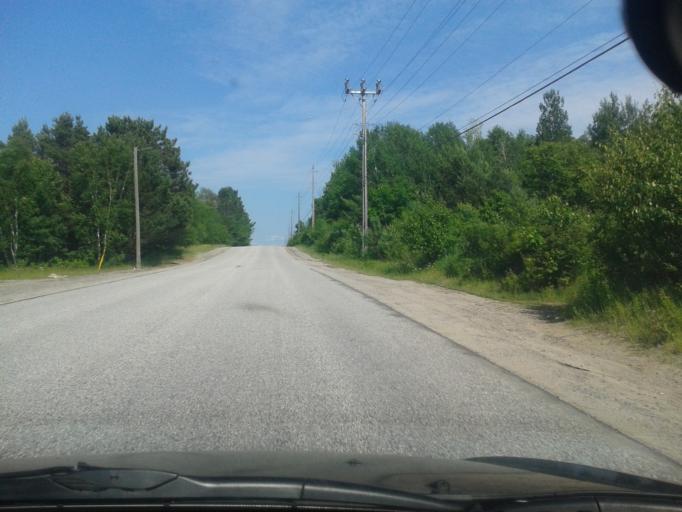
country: CA
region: Ontario
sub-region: Nipissing District
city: North Bay
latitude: 46.3470
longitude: -79.4792
